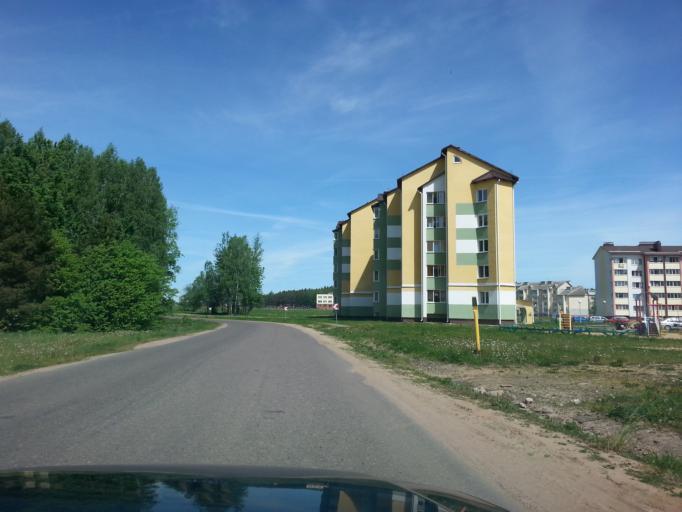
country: BY
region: Minsk
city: Narach
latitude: 54.9144
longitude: 26.6968
